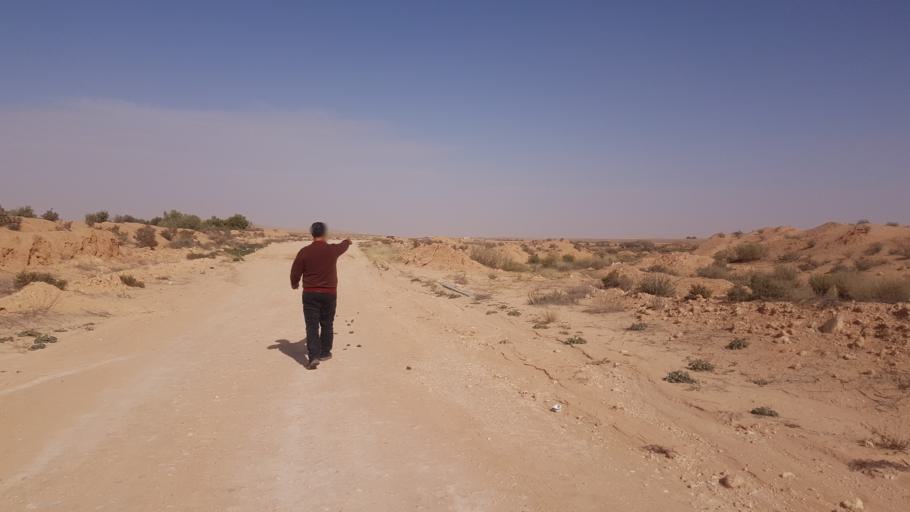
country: TN
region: Qabis
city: El Hamma
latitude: 33.6627
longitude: 9.7350
